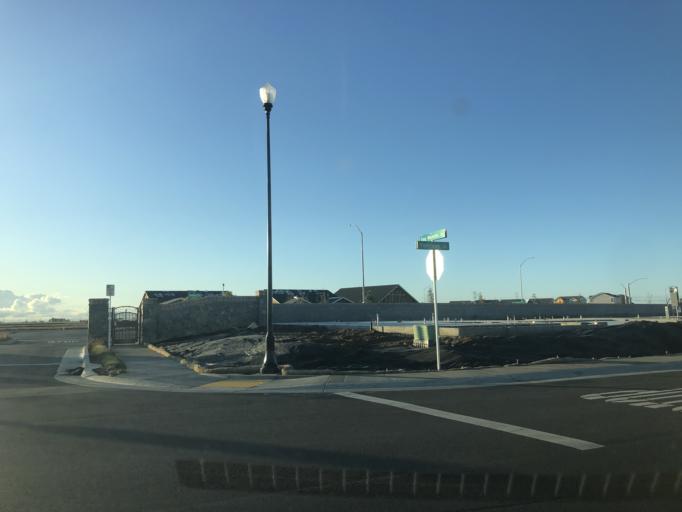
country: US
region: California
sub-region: Sacramento County
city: Antelope
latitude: 38.7587
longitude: -121.3628
